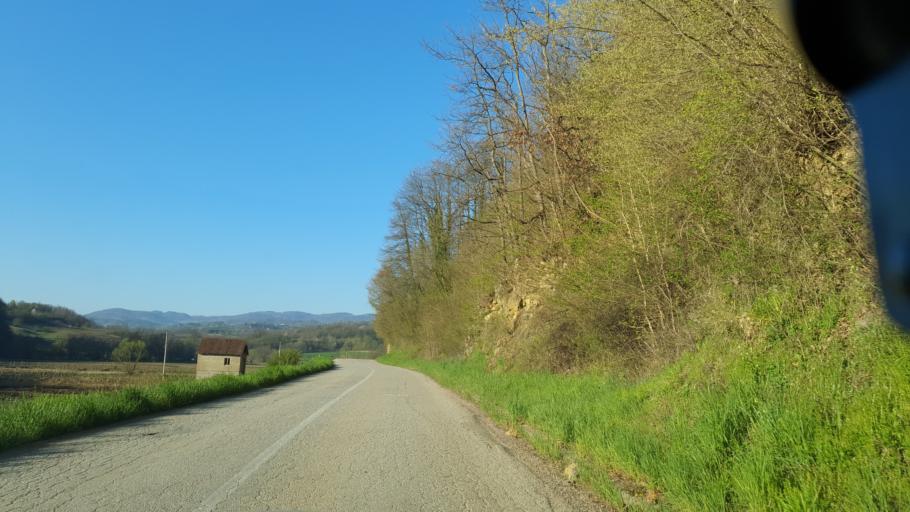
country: RS
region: Central Serbia
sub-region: Kolubarski Okrug
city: Osecina
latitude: 44.3532
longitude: 19.5236
